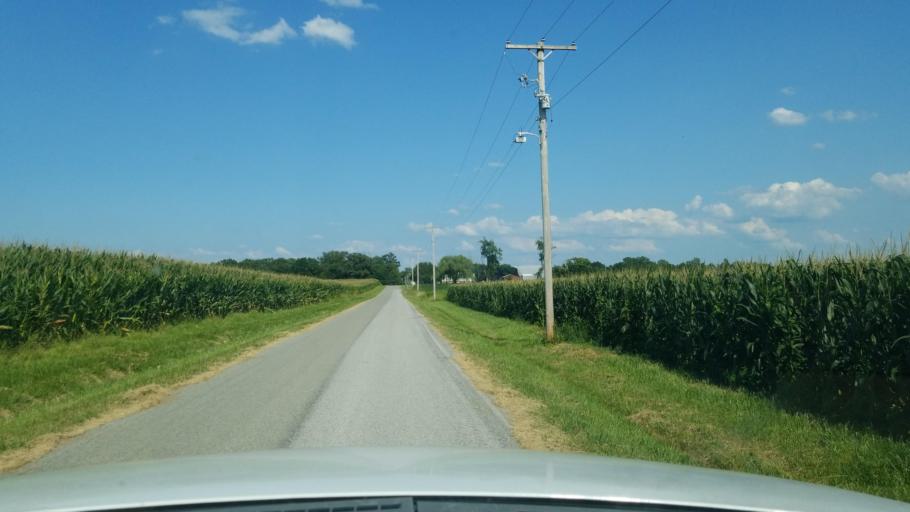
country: US
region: Illinois
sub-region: Saline County
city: Harrisburg
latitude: 37.7865
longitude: -88.4976
